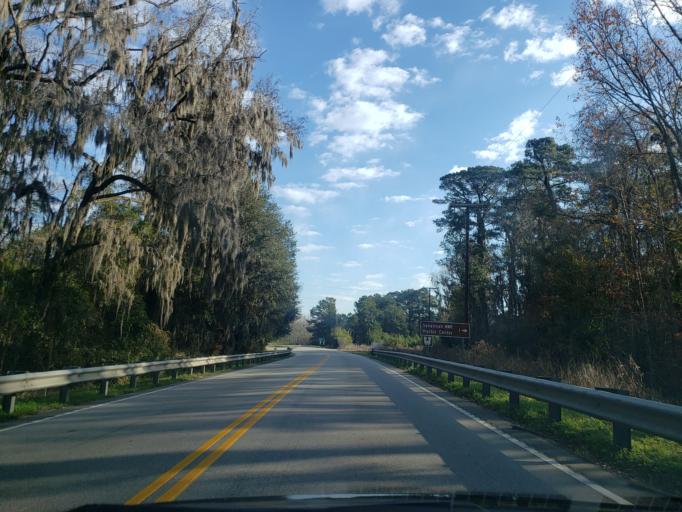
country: US
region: Georgia
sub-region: Chatham County
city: Port Wentworth
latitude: 32.1789
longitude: -81.0818
